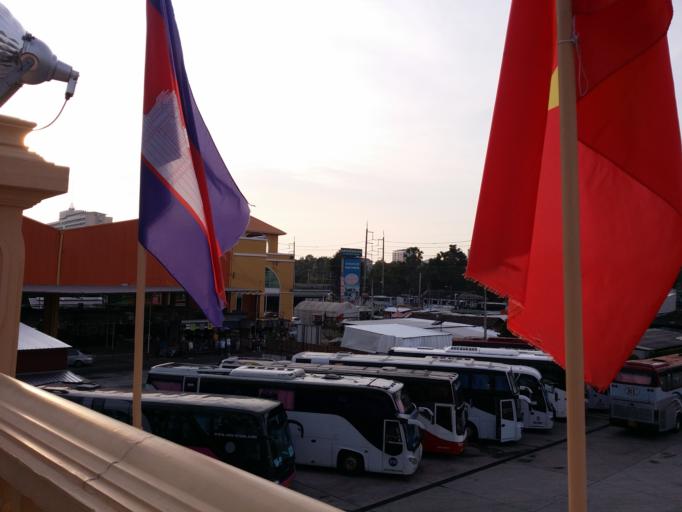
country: TH
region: Chon Buri
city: Phatthaya
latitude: 12.9052
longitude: 100.8773
